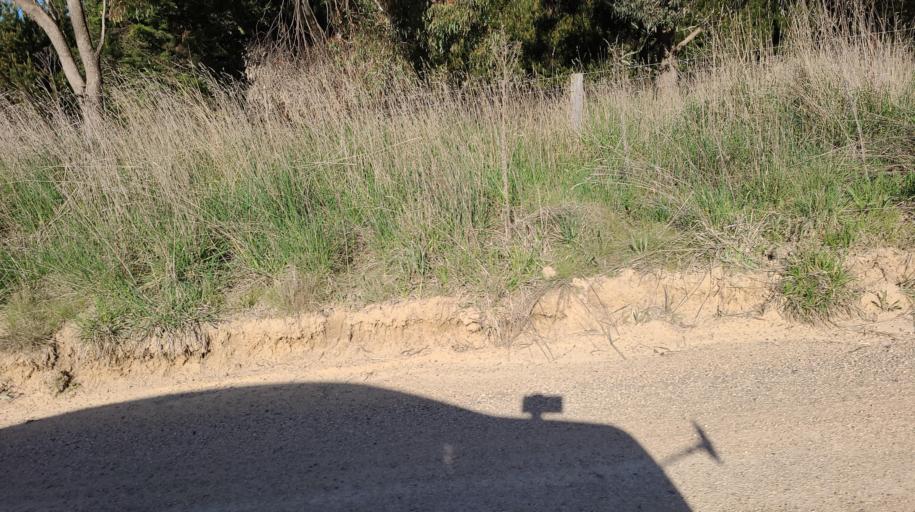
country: AU
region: New South Wales
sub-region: Blayney
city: Millthorpe
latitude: -33.4089
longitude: 149.3068
